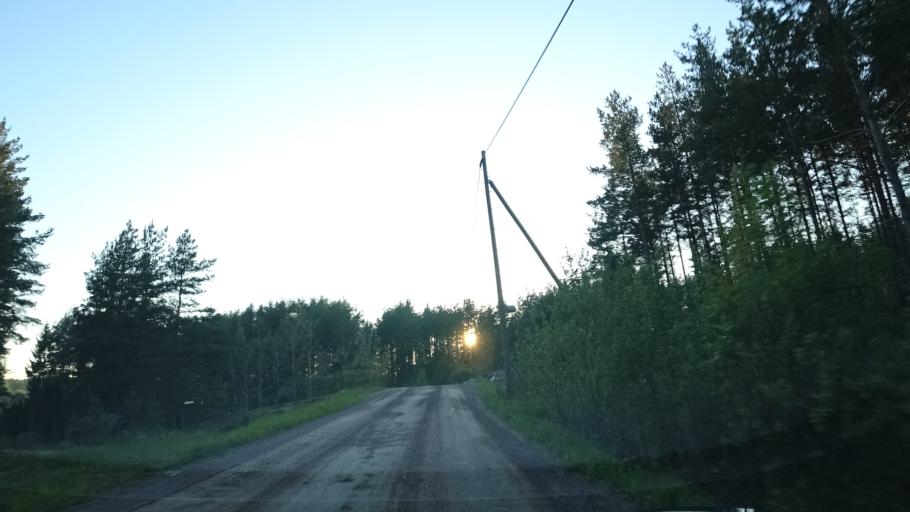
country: FI
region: Uusimaa
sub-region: Helsinki
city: Siuntio
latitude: 60.0641
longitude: 24.2230
